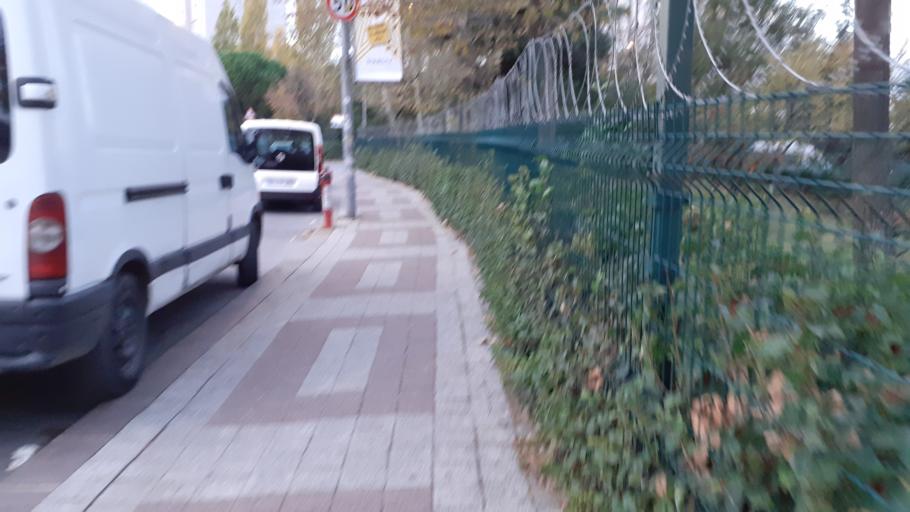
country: TR
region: Istanbul
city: Mahmutbey
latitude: 41.0578
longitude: 28.7896
